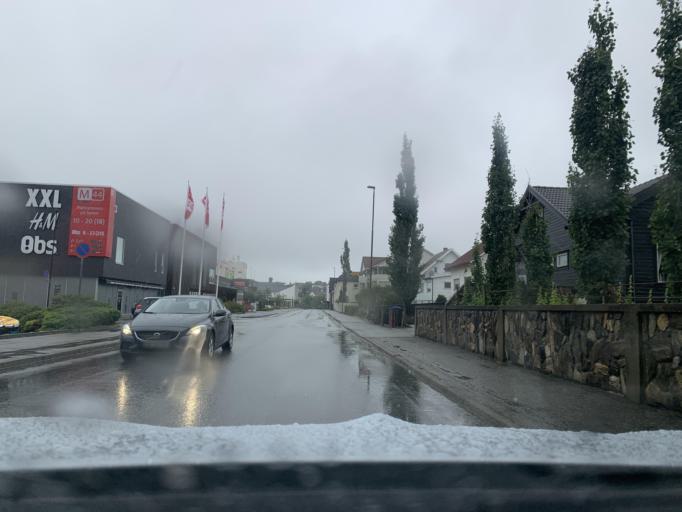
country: NO
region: Rogaland
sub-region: Time
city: Bryne
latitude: 58.7343
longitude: 5.6400
